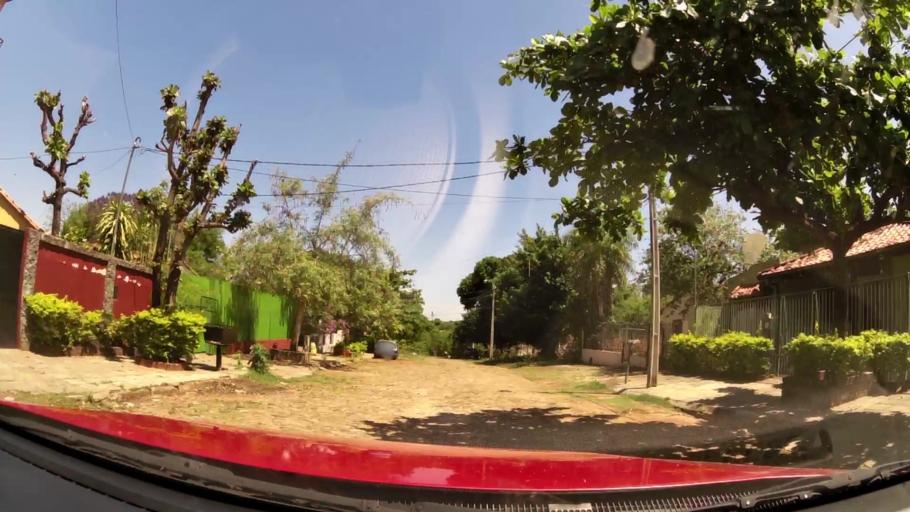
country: PY
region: Central
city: Colonia Mariano Roque Alonso
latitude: -25.2362
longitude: -57.5516
